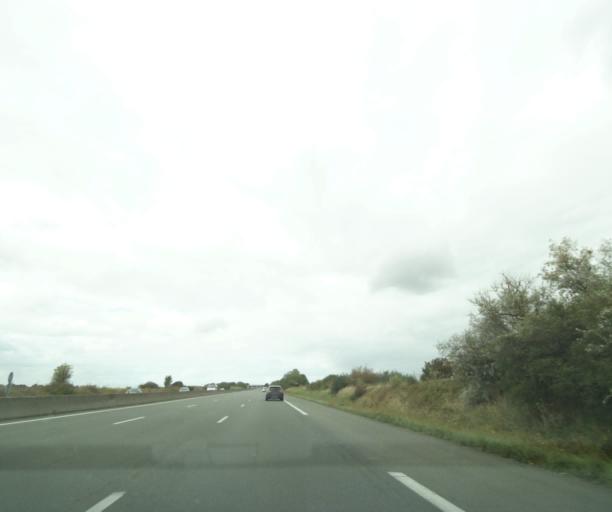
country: FR
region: Ile-de-France
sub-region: Departement de l'Essonne
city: Corbreuse
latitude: 48.4733
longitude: 1.9132
